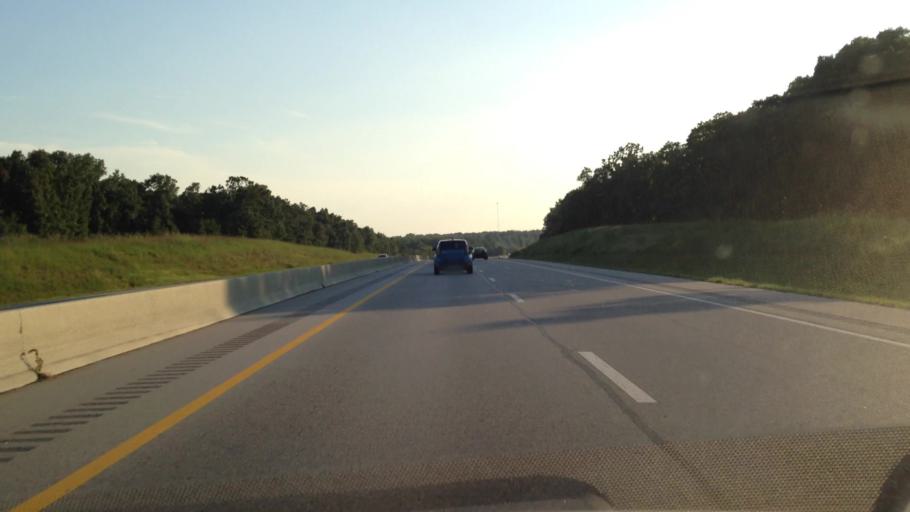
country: US
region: Kansas
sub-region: Cherokee County
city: Baxter Springs
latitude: 36.9473
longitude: -94.6799
